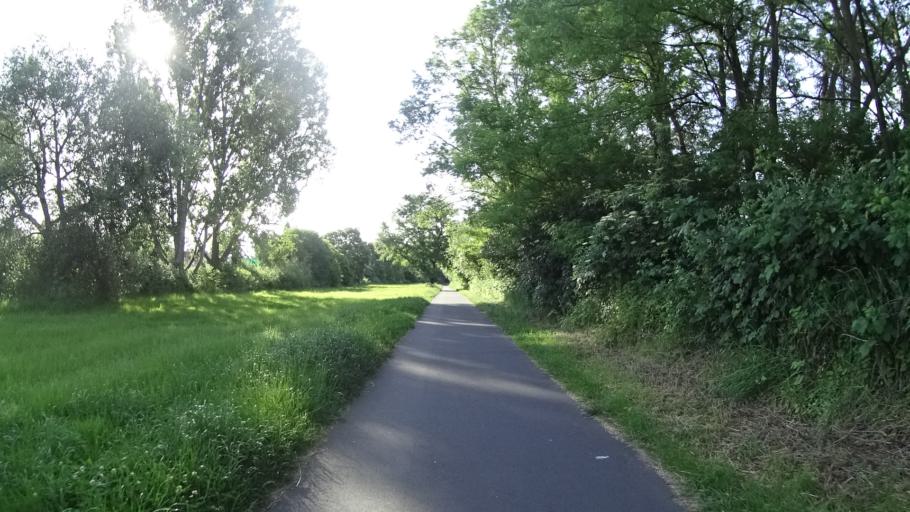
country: DE
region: Hesse
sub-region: Regierungsbezirk Darmstadt
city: Grosskrotzenburg
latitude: 50.0779
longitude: 8.9819
